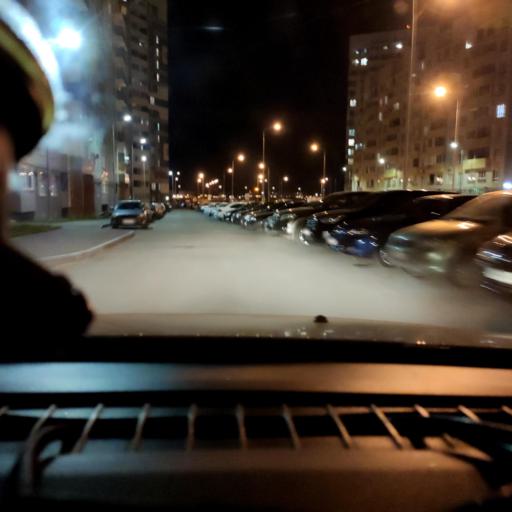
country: RU
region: Samara
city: Samara
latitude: 53.0937
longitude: 50.1614
